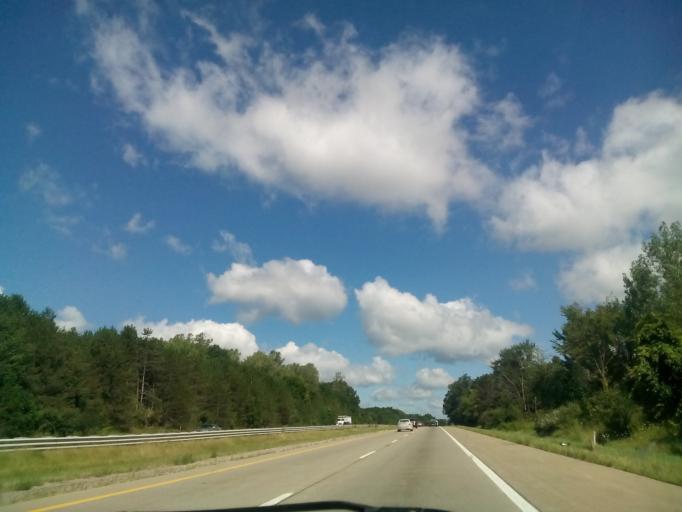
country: US
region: Michigan
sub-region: Genesee County
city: Lake Fenton
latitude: 42.8417
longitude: -83.7366
